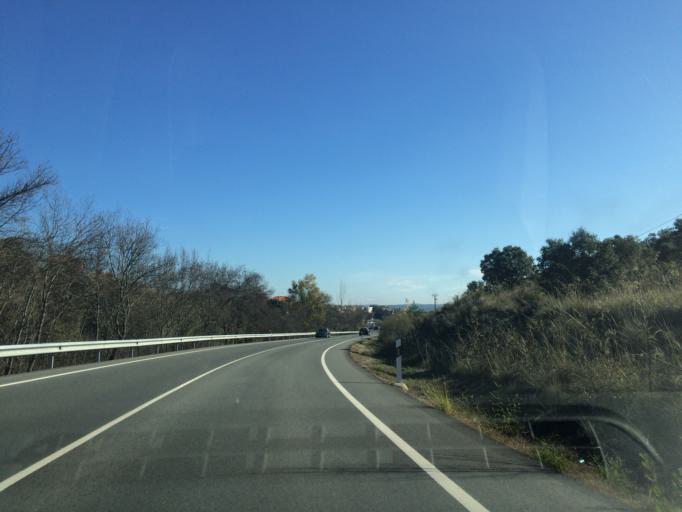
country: ES
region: Madrid
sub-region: Provincia de Madrid
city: Guadalix de la Sierra
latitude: 40.7831
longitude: -3.7129
